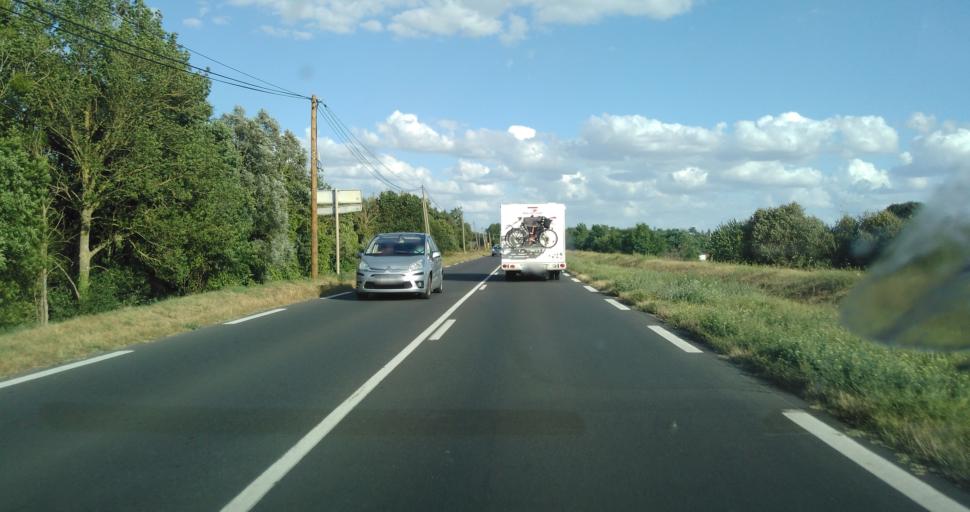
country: FR
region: Centre
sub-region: Departement d'Indre-et-Loire
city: Vouvray
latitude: 47.4003
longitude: 0.8155
